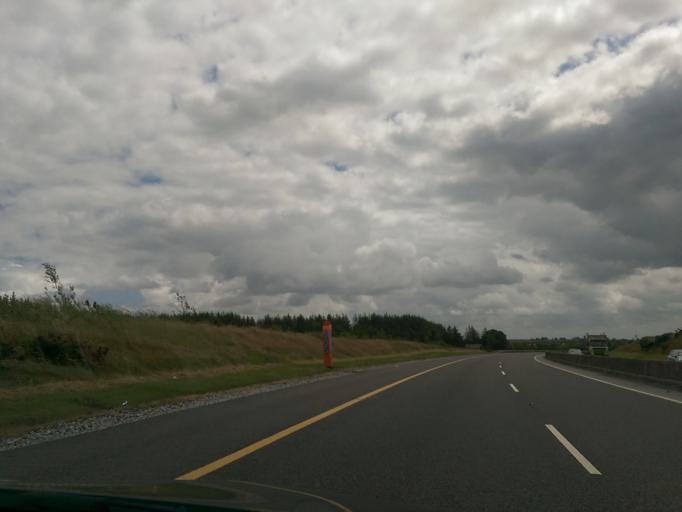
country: IE
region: Munster
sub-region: County Cork
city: Mitchelstown
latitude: 52.2160
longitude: -8.2803
